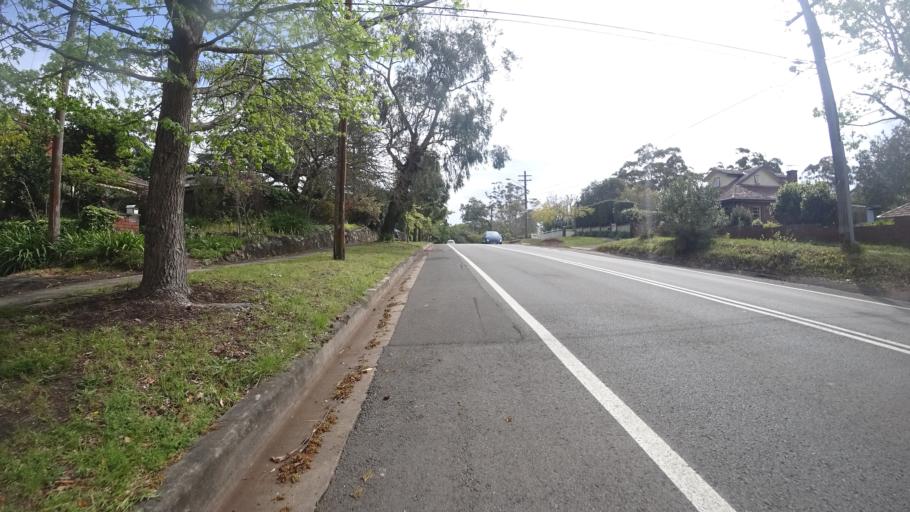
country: AU
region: New South Wales
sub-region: City of Sydney
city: Pymble
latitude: -33.7335
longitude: 151.1377
